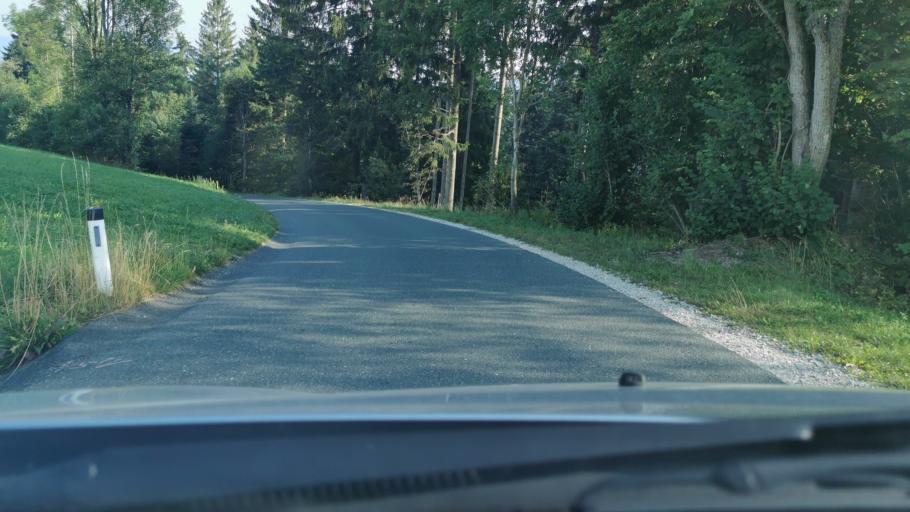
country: AT
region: Styria
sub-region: Politischer Bezirk Weiz
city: Fischbach
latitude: 47.3890
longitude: 15.6488
